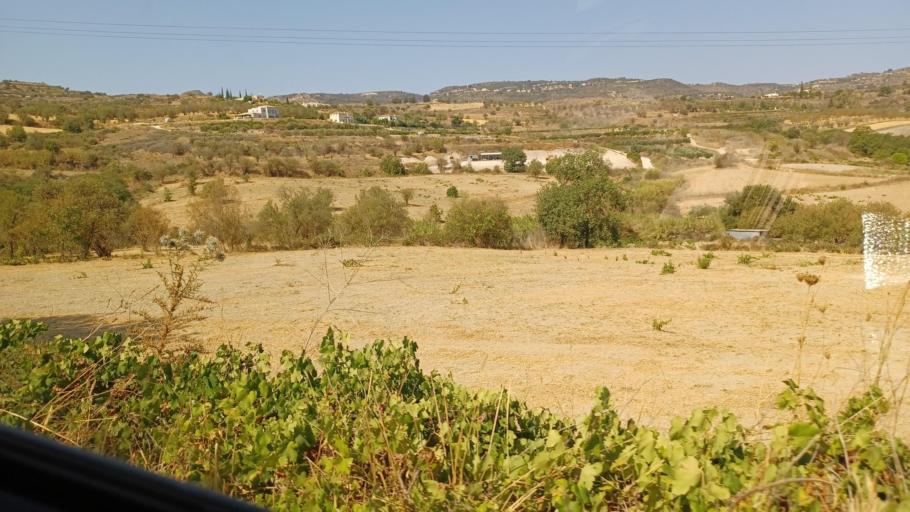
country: CY
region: Pafos
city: Tala
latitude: 34.9146
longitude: 32.4786
